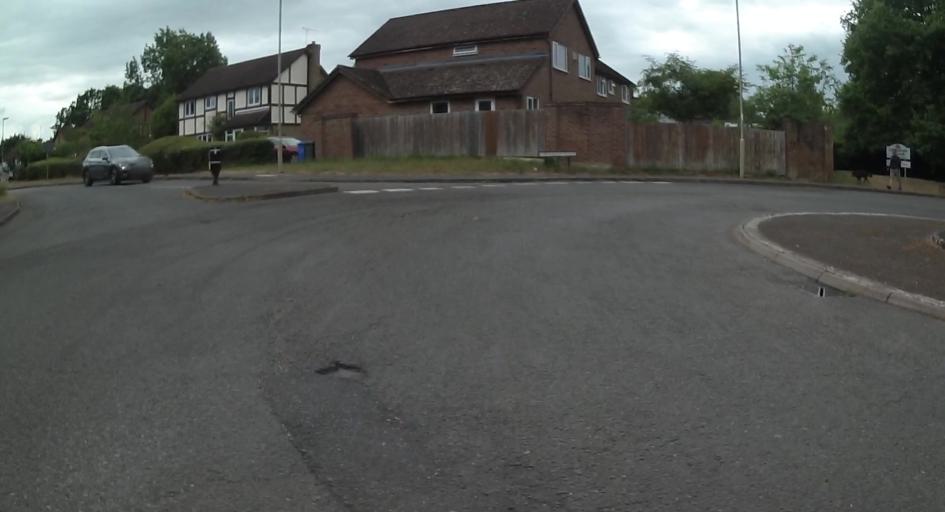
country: GB
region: England
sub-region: Hampshire
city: Fleet
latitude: 51.2640
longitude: -0.8528
